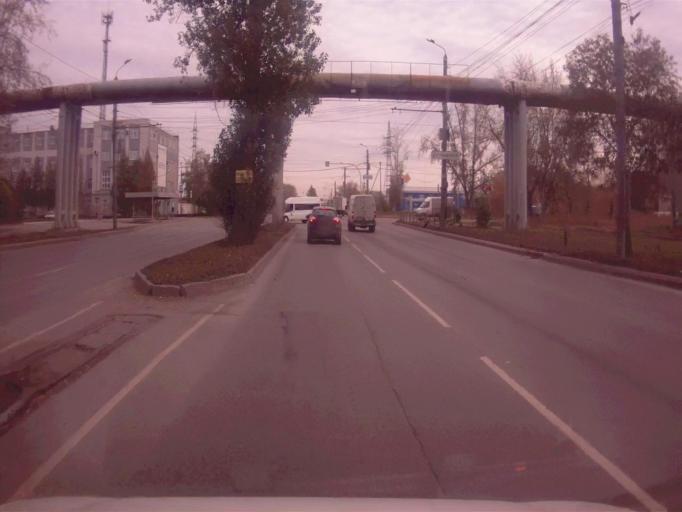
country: RU
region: Chelyabinsk
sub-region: Gorod Chelyabinsk
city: Chelyabinsk
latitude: 55.1344
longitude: 61.4669
